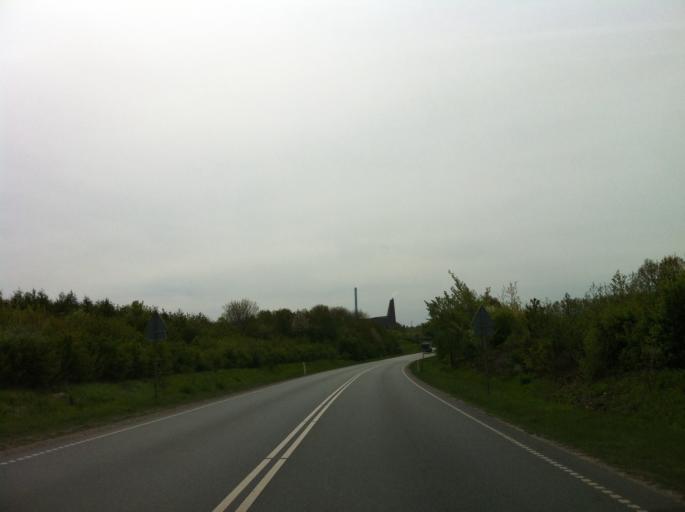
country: DK
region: Zealand
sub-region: Roskilde Kommune
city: Roskilde
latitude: 55.6596
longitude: 12.1181
